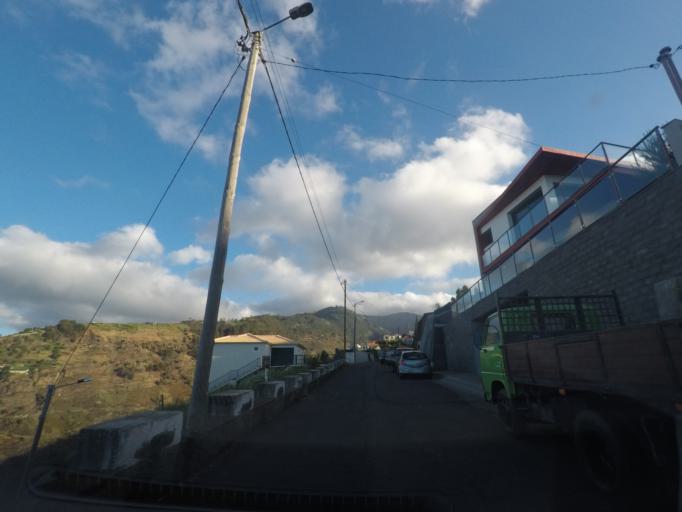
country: PT
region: Madeira
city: Ponta do Sol
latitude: 32.6918
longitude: -17.0879
